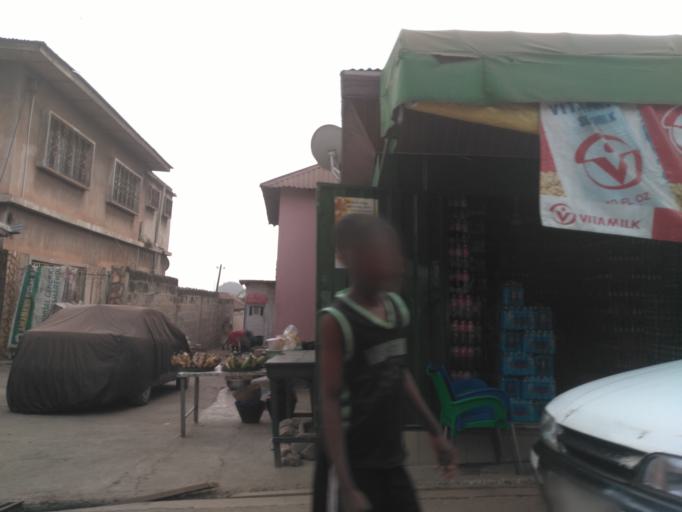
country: GH
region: Ashanti
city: Kumasi
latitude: 6.6896
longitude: -1.6014
